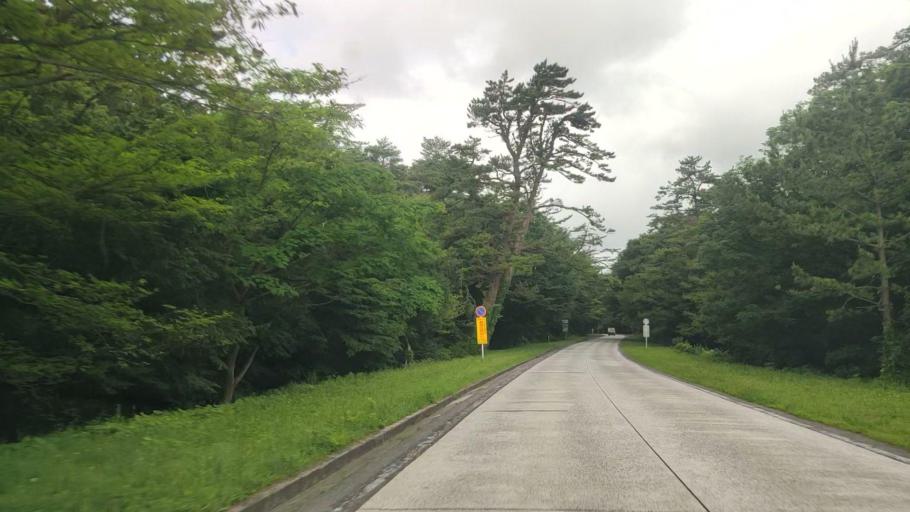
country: JP
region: Tottori
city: Yonago
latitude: 35.3979
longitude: 133.5112
